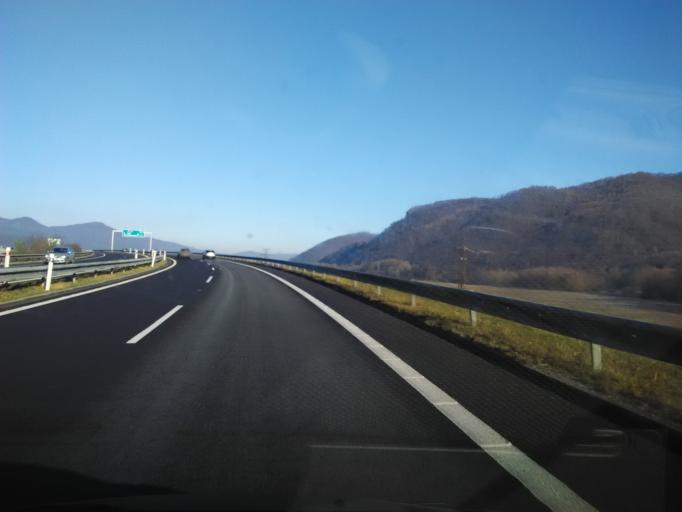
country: SK
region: Banskobystricky
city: Zarnovica
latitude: 48.4993
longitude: 18.7330
